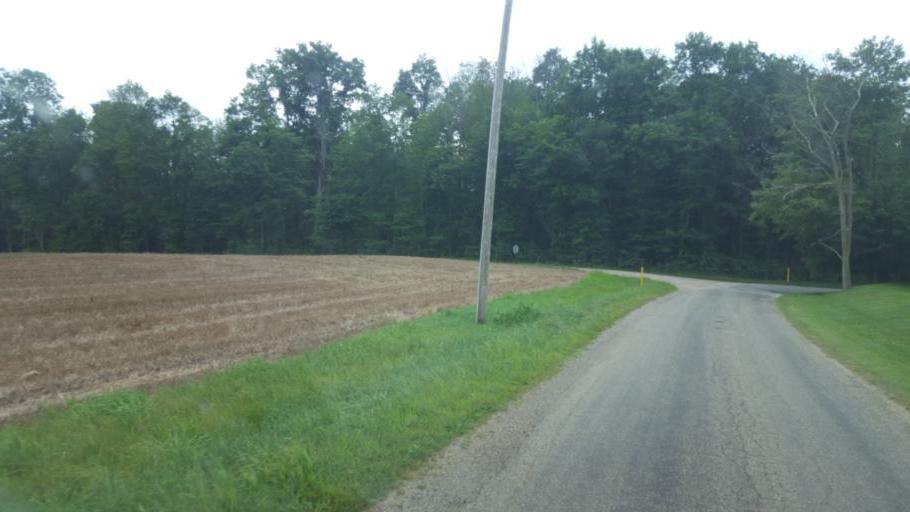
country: US
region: Ohio
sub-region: Richland County
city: Lexington
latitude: 40.6668
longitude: -82.6388
